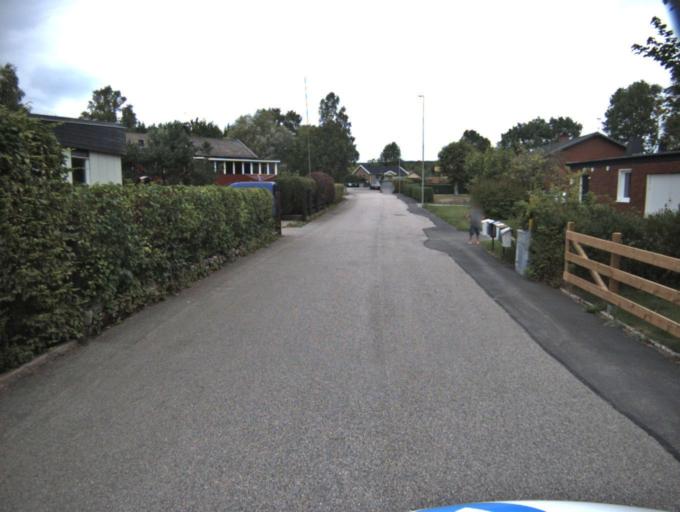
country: SE
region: Vaestra Goetaland
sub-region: Boras Kommun
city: Dalsjofors
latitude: 57.8287
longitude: 13.1957
